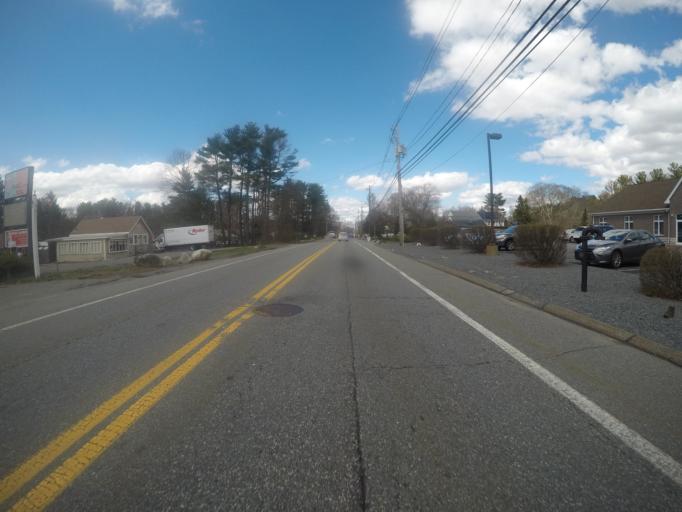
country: US
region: Massachusetts
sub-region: Plymouth County
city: West Bridgewater
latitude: 42.0151
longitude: -71.0667
